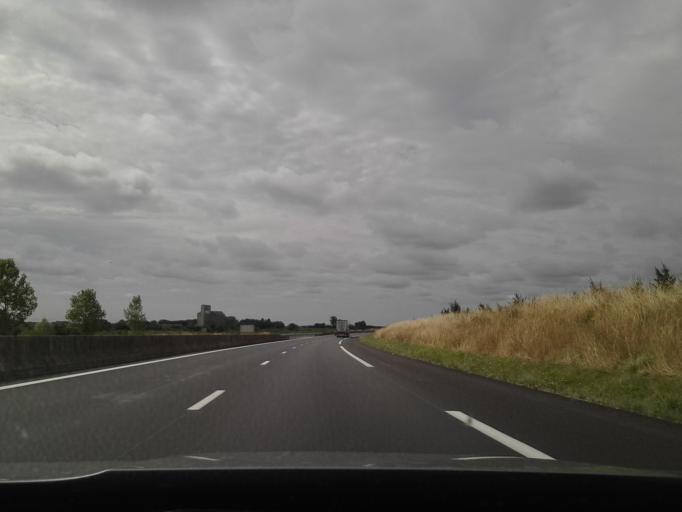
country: FR
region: Lower Normandy
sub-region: Departement de l'Orne
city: Valframbert
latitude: 48.4701
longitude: 0.1252
